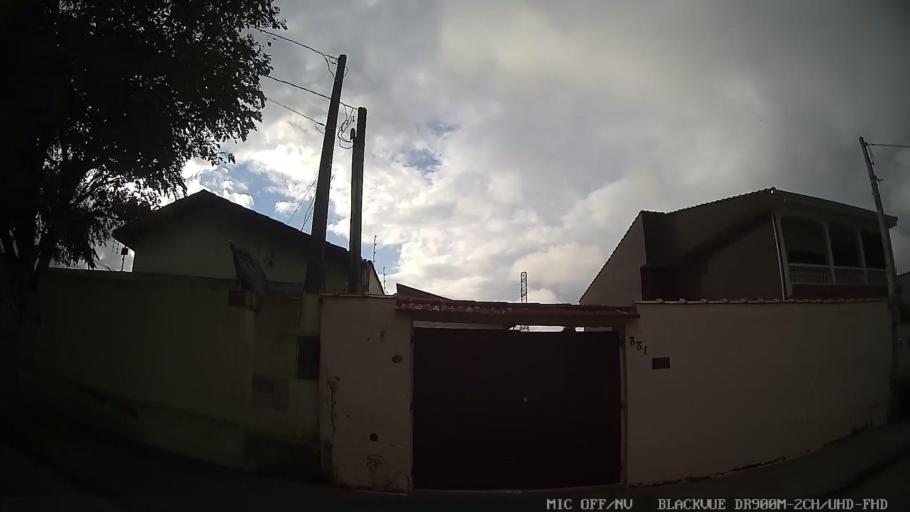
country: BR
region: Sao Paulo
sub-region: Itanhaem
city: Itanhaem
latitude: -24.1776
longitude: -46.7837
